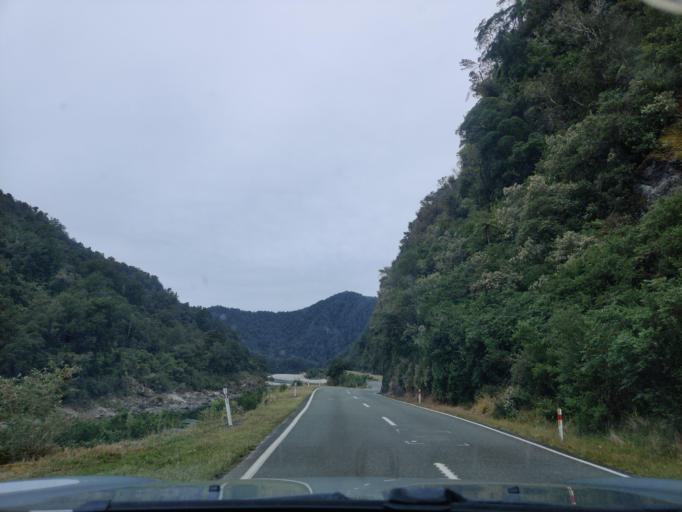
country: NZ
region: West Coast
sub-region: Buller District
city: Westport
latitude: -41.8581
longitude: 171.7622
